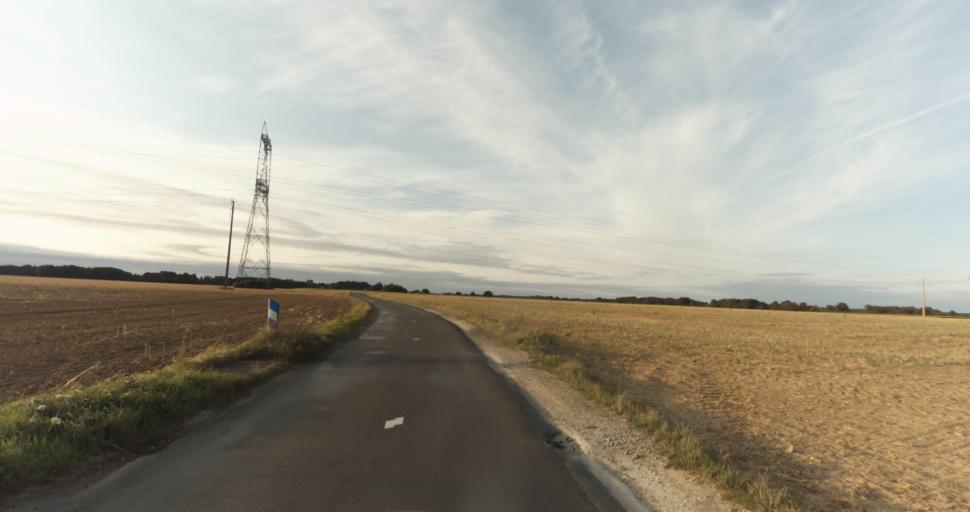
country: FR
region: Haute-Normandie
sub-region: Departement de l'Eure
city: Marcilly-sur-Eure
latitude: 48.8547
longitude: 1.2744
